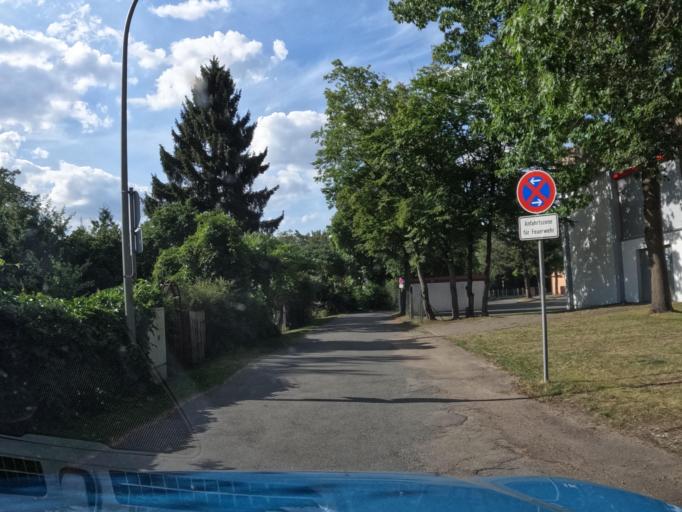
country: DE
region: Bavaria
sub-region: Upper Palatinate
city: Nabburg
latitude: 49.4499
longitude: 12.1835
